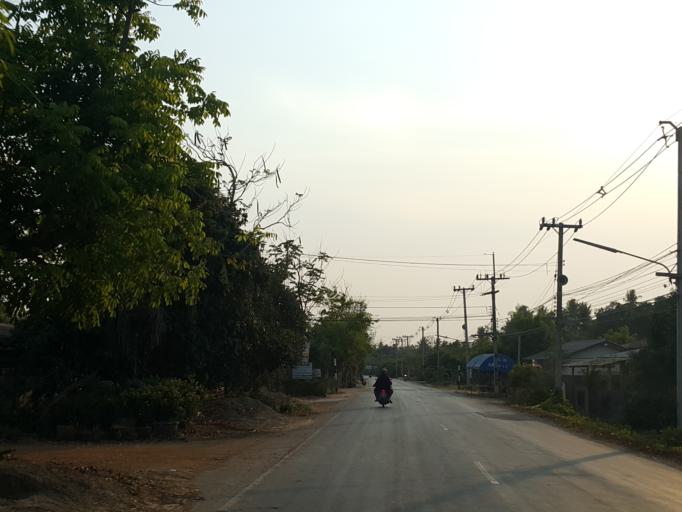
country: TH
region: Sukhothai
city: Si Samrong
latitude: 17.2127
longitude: 99.8737
